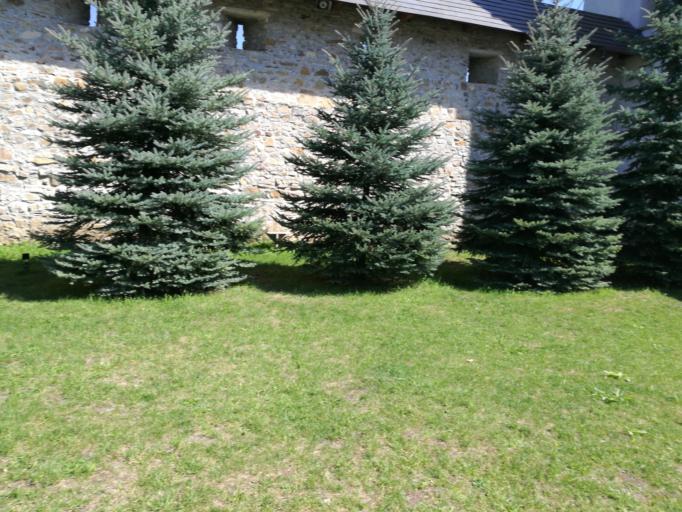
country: RO
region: Suceava
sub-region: Comuna Putna
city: Putna
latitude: 47.8665
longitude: 25.5969
